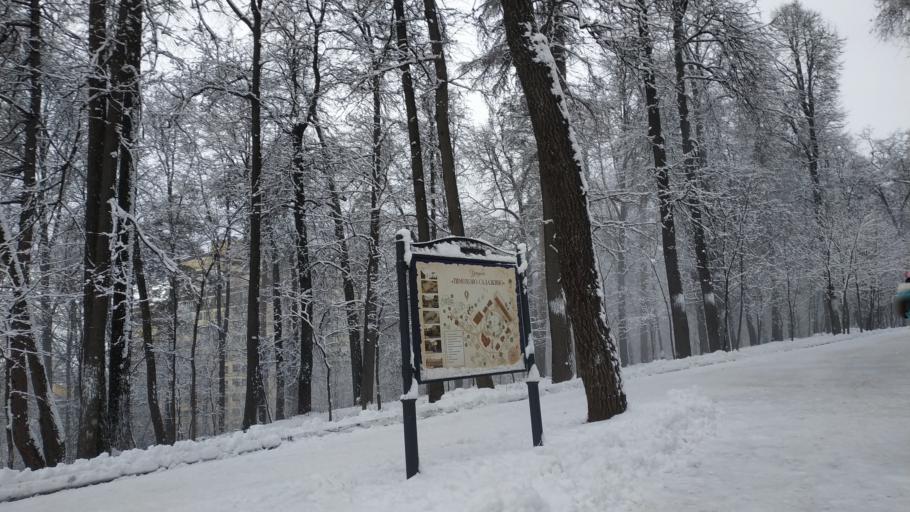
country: RU
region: Moskovskaya
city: Vidnoye
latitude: 55.5512
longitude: 37.6920
